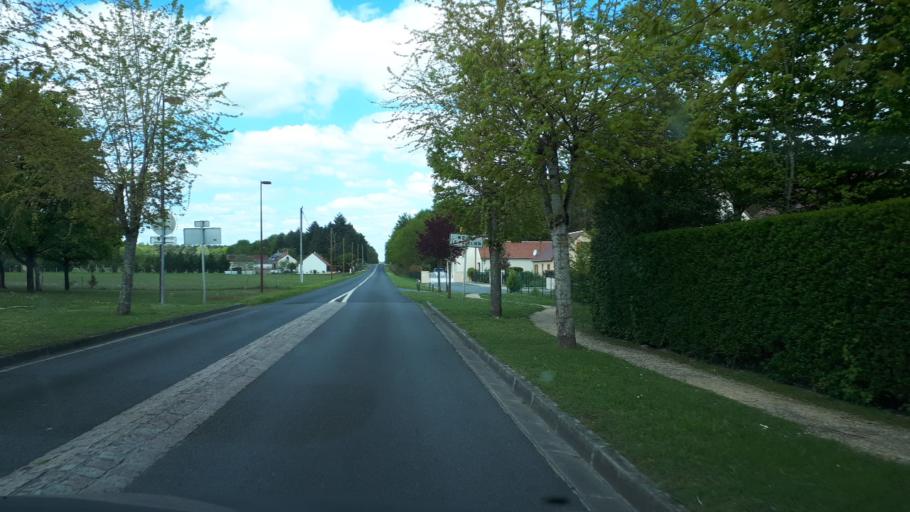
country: FR
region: Centre
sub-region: Departement du Loir-et-Cher
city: Nouan-le-Fuzelier
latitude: 47.5347
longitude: 2.0267
